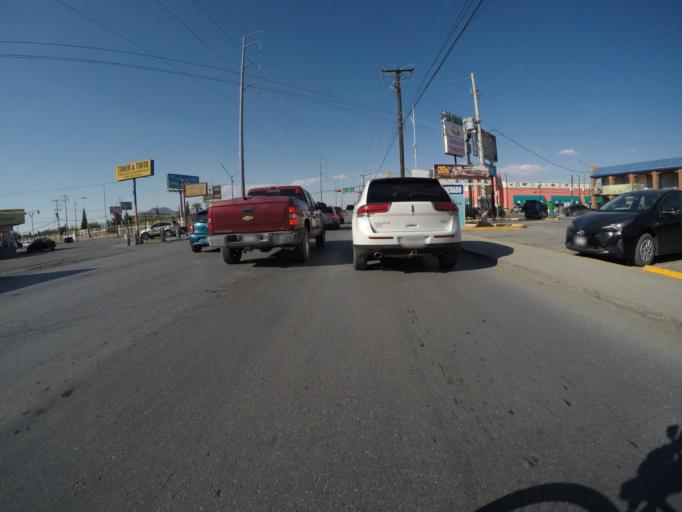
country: MX
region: Chihuahua
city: Ciudad Juarez
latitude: 31.7285
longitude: -106.4415
